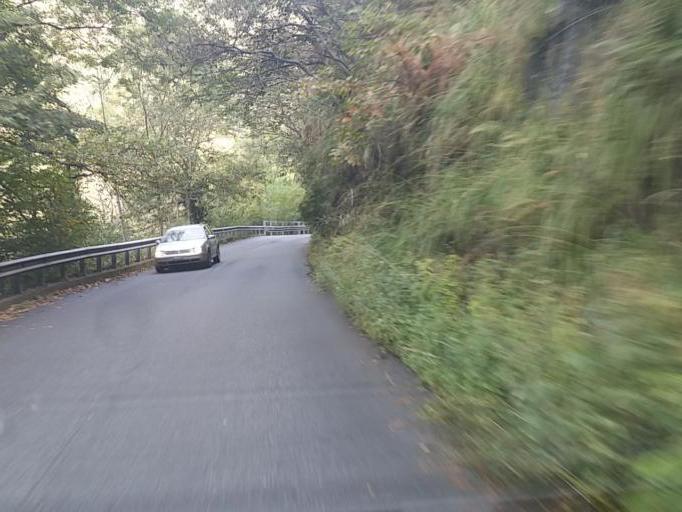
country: IT
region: Piedmont
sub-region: Provincia Verbano-Cusio-Ossola
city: Cavaglio-Spoccia
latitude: 46.0648
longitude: 8.6583
